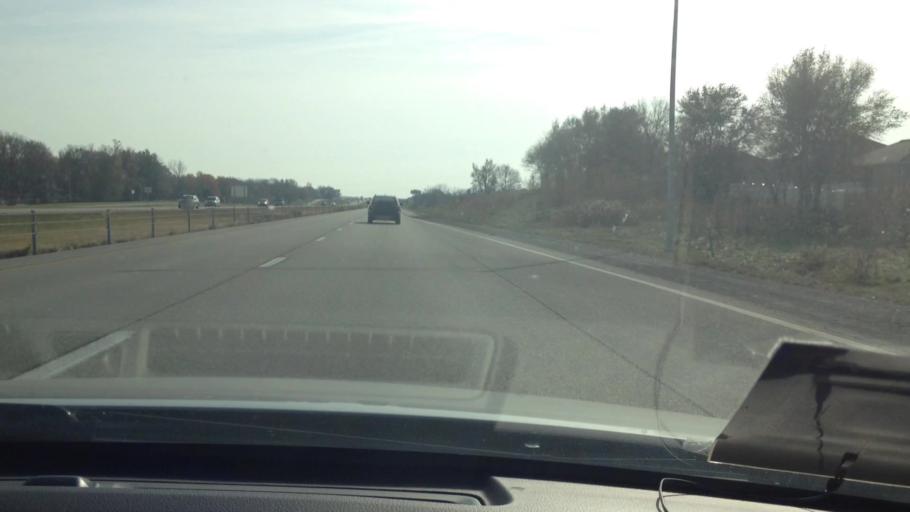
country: US
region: Missouri
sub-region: Cass County
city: Peculiar
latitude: 38.7197
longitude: -94.4521
